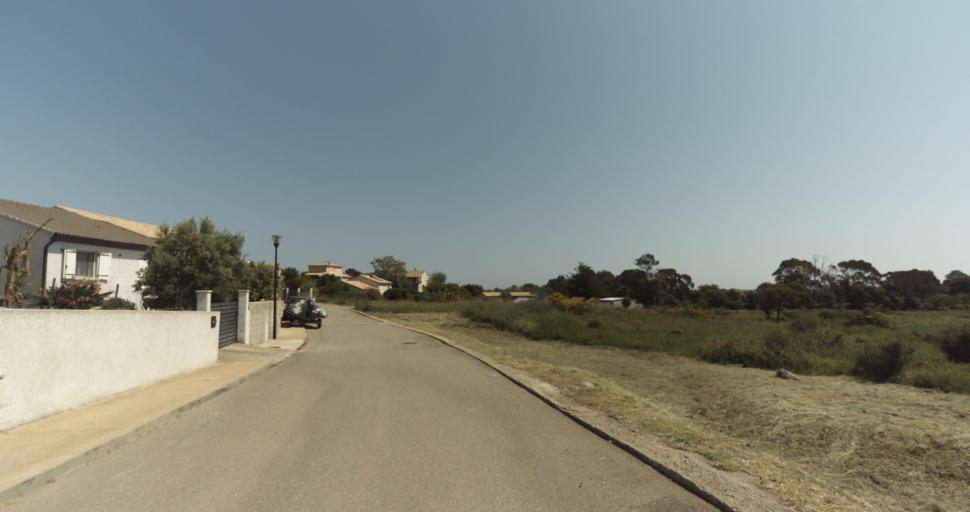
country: FR
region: Corsica
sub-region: Departement de la Haute-Corse
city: Biguglia
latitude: 42.6024
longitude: 9.4318
